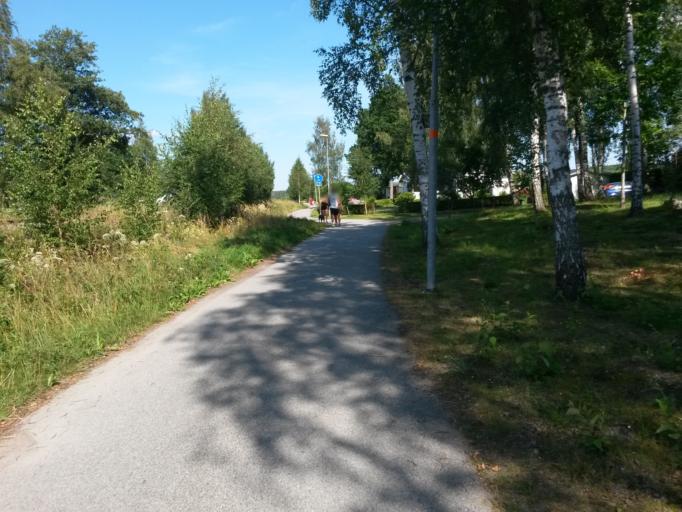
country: SE
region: Vaestra Goetaland
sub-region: Gotene Kommun
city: Kallby
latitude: 58.4953
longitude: 13.2761
